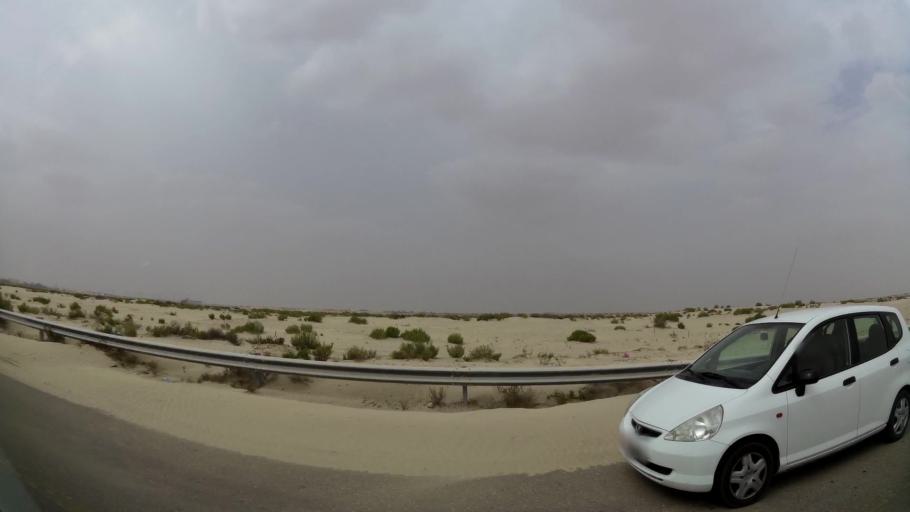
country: AE
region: Abu Dhabi
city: Abu Dhabi
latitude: 24.3845
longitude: 54.6785
